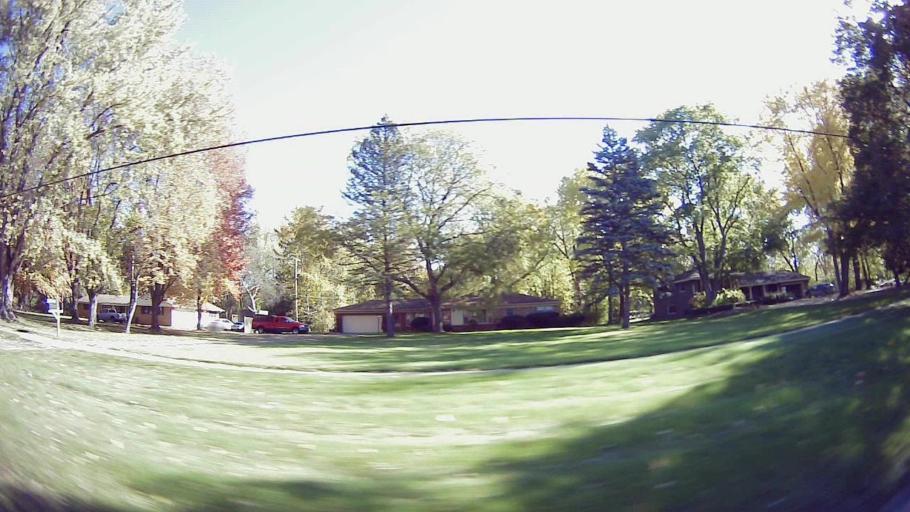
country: US
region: Michigan
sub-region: Wayne County
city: Livonia
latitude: 42.4080
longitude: -83.3740
